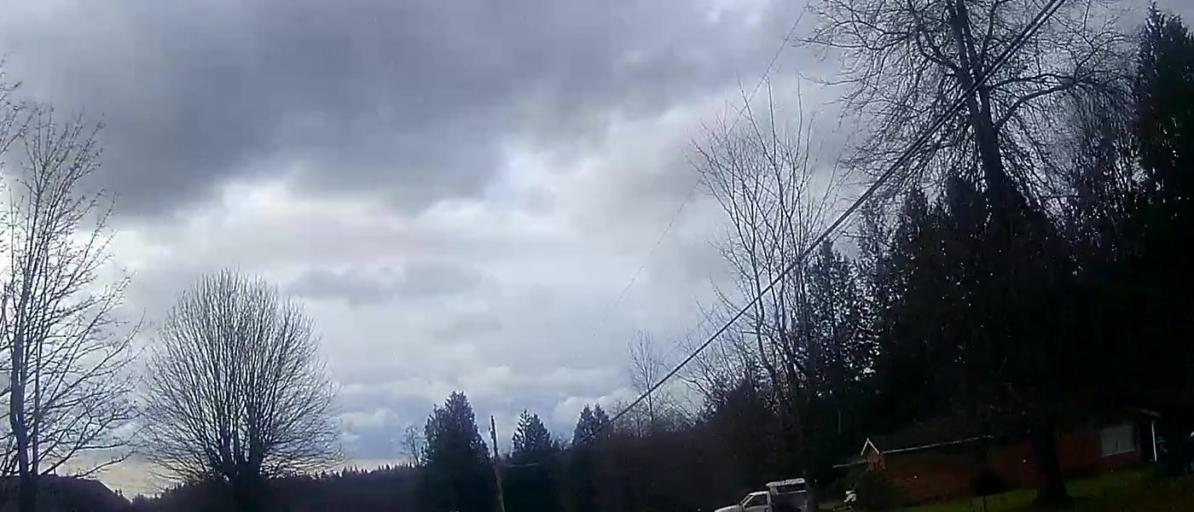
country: US
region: Washington
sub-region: Skagit County
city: Sedro-Woolley
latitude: 48.5794
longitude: -122.2948
